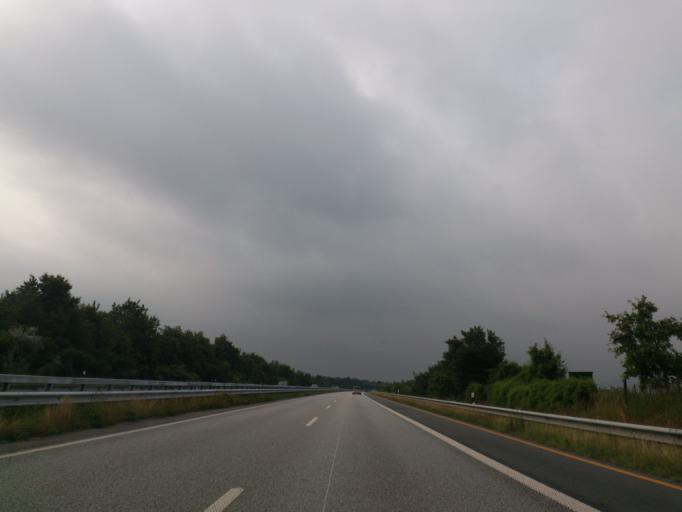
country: DE
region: Schleswig-Holstein
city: Tensbuttel-Rost
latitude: 54.1059
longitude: 9.2637
